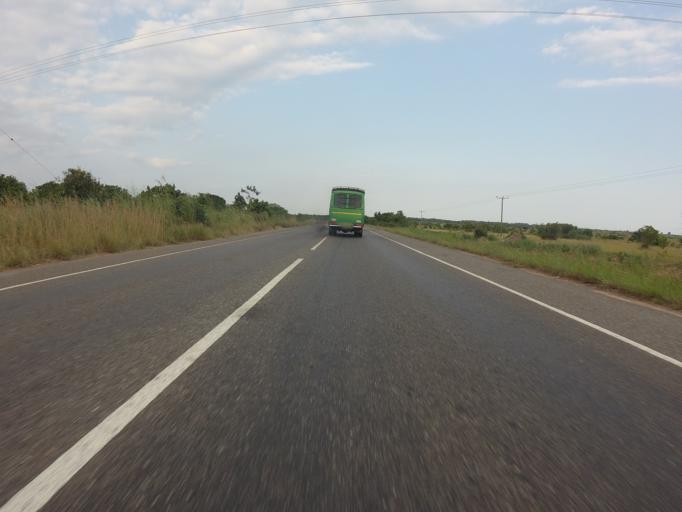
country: GH
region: Volta
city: Anloga
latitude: 6.0901
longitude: 0.5307
